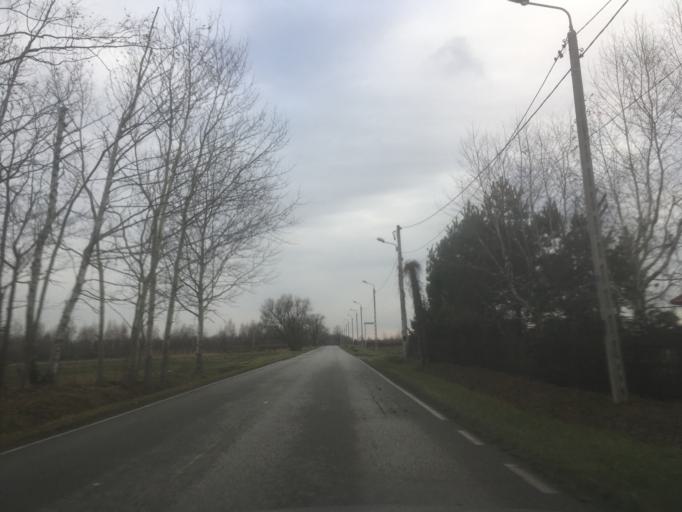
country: PL
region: Masovian Voivodeship
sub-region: Powiat piaseczynski
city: Lesznowola
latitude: 52.0470
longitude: 20.9634
